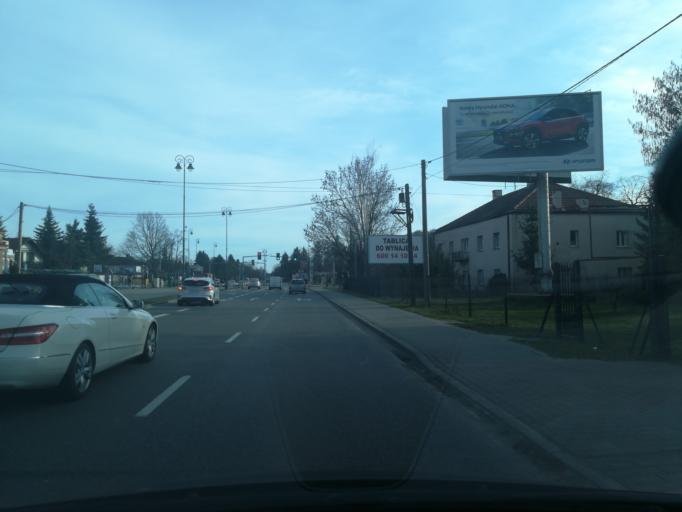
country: PL
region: Masovian Voivodeship
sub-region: Powiat piaseczynski
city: Konstancin-Jeziorna
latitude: 52.1037
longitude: 21.1140
